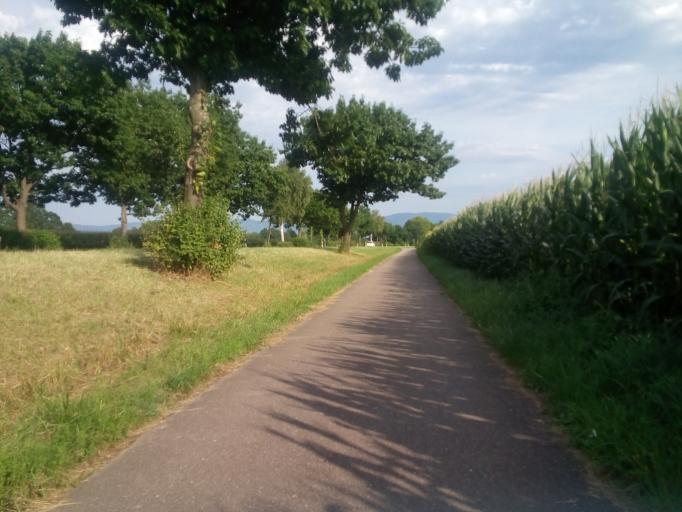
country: DE
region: Baden-Wuerttemberg
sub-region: Karlsruhe Region
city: Lichtenau
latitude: 48.7195
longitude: 8.0304
